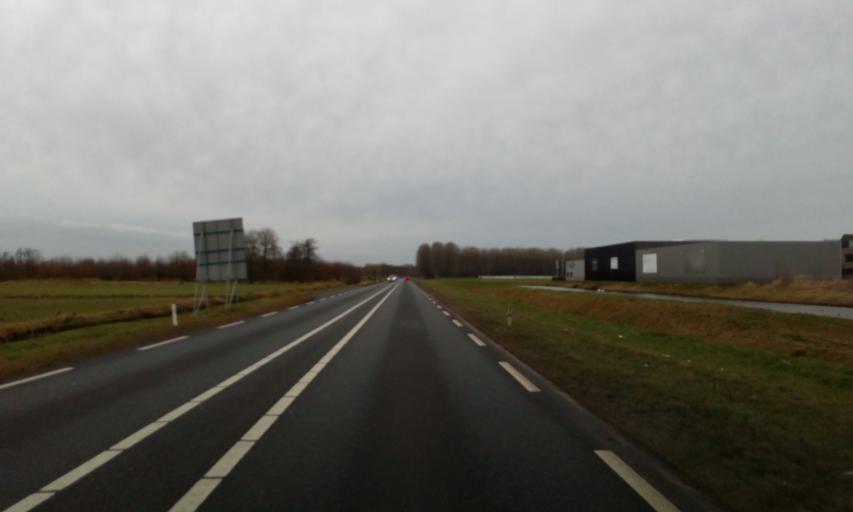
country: NL
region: Gelderland
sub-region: Gemeente Zaltbommel
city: Nederhemert-Noord
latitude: 51.7944
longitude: 5.2022
